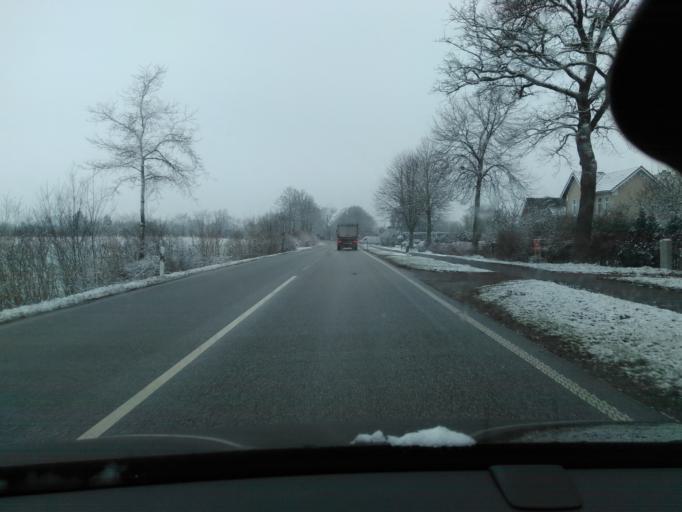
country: DE
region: Schleswig-Holstein
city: Travenhorst
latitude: 53.9993
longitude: 10.4973
